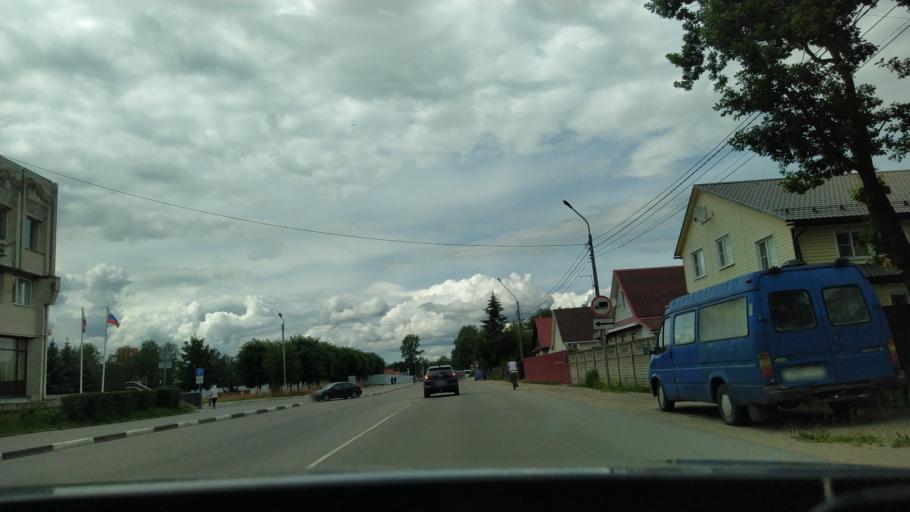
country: RU
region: Leningrad
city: Kirovsk
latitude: 59.8815
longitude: 30.9879
